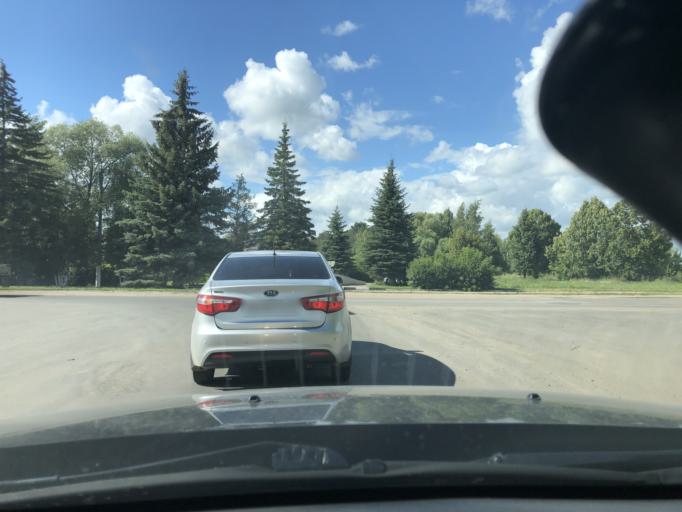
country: RU
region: Tula
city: Donskoy
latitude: 53.9697
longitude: 38.3570
